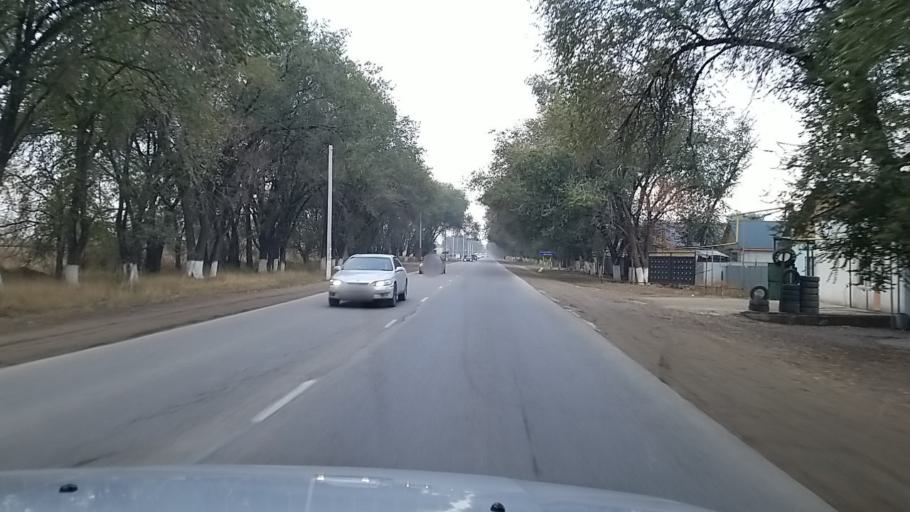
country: KZ
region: Almaty Oblysy
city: Burunday
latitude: 43.3549
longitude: 76.8094
